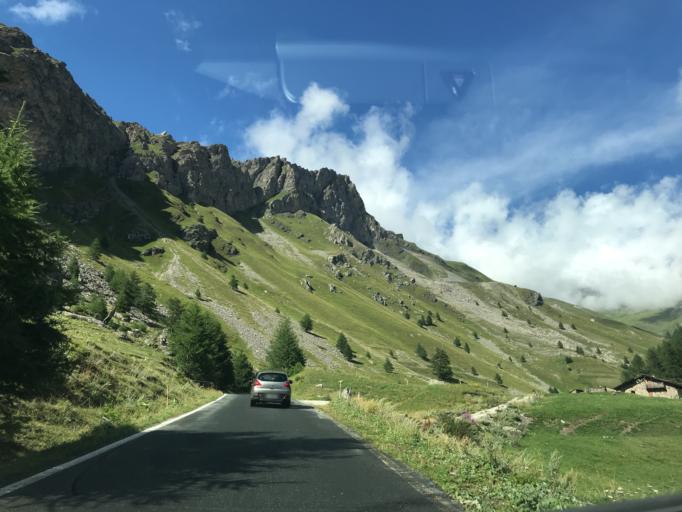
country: IT
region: Piedmont
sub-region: Provincia di Cuneo
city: Pontechianale
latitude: 44.6600
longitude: 6.9911
